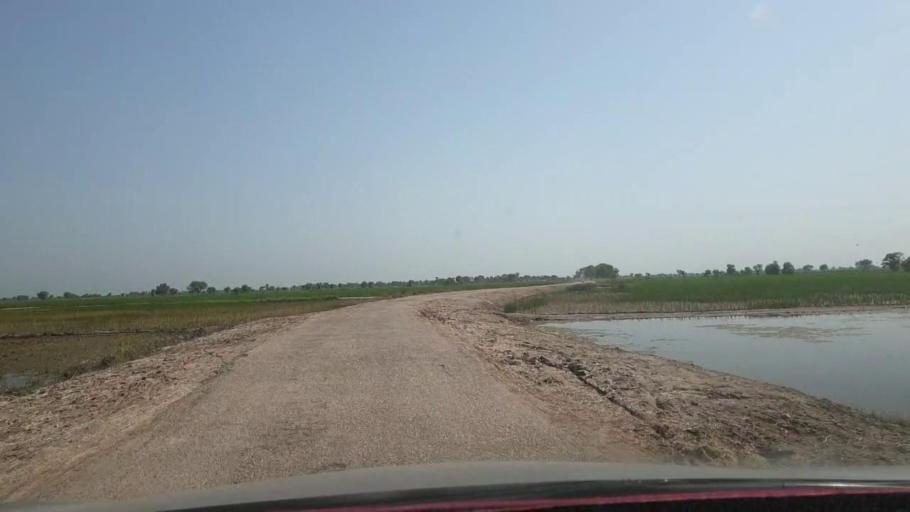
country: PK
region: Sindh
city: Nasirabad
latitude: 27.3673
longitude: 67.8532
